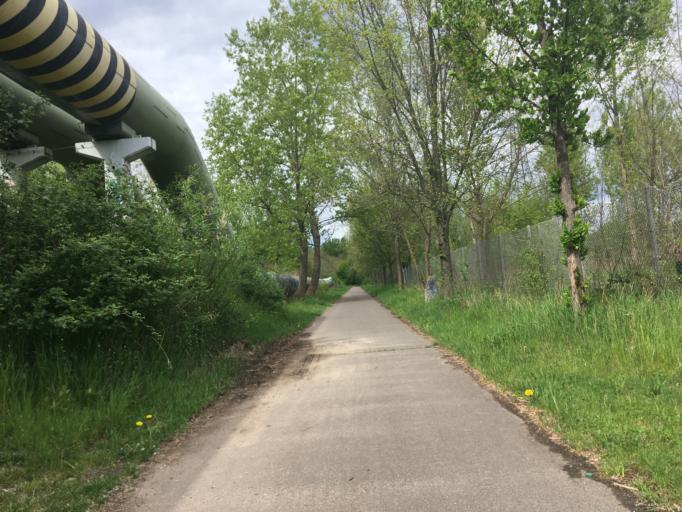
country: DE
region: Berlin
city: Falkenberg
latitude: 52.5475
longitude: 13.5315
